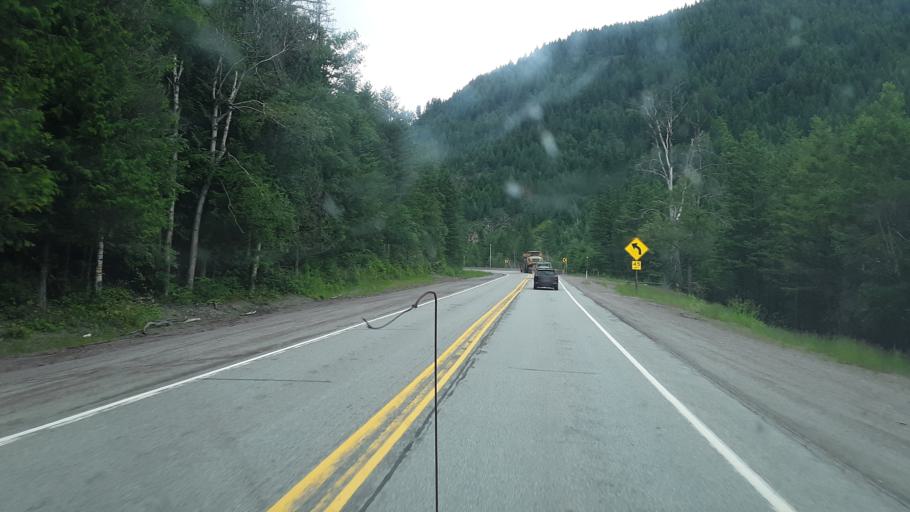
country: US
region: Montana
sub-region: Flathead County
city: Columbia Falls
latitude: 48.4998
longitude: -113.9291
